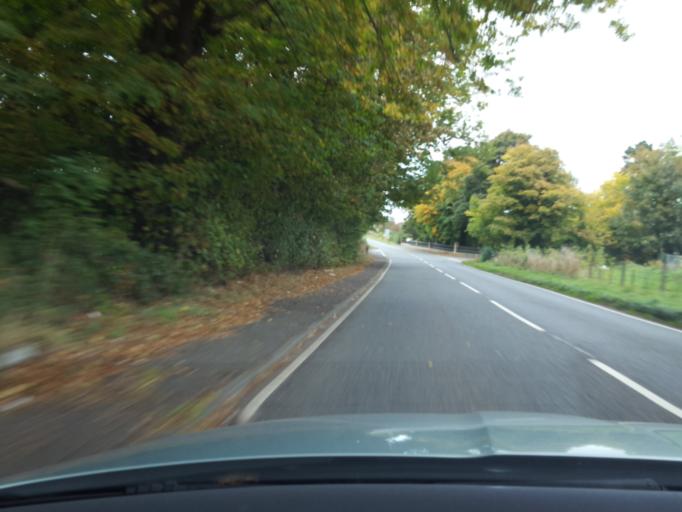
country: GB
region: Scotland
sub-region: Fife
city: Pathhead
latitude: 55.8701
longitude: -2.9907
